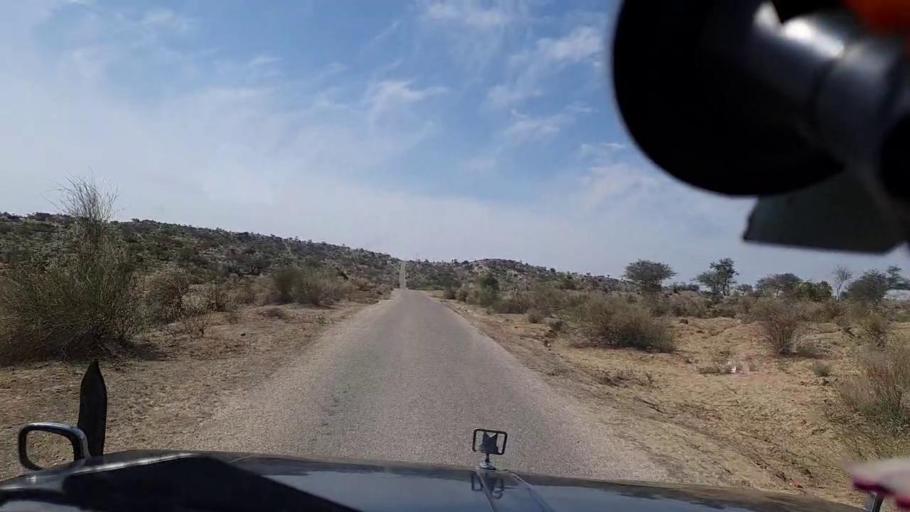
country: PK
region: Sindh
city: Diplo
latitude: 24.3892
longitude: 69.5886
